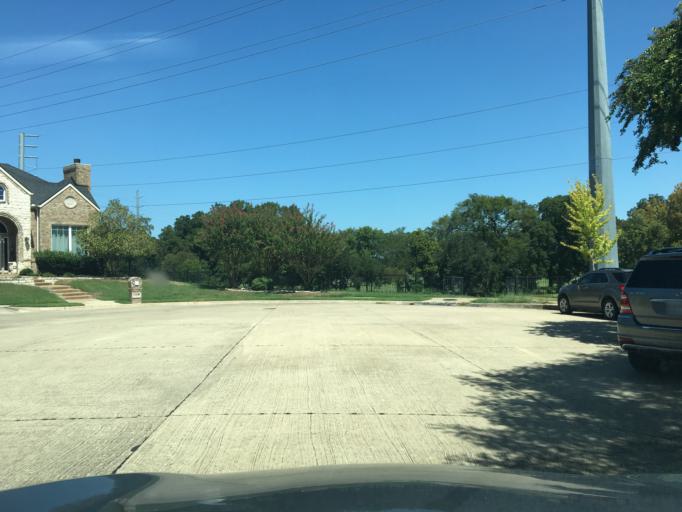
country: US
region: Texas
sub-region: Dallas County
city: Sachse
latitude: 32.9662
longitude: -96.6263
